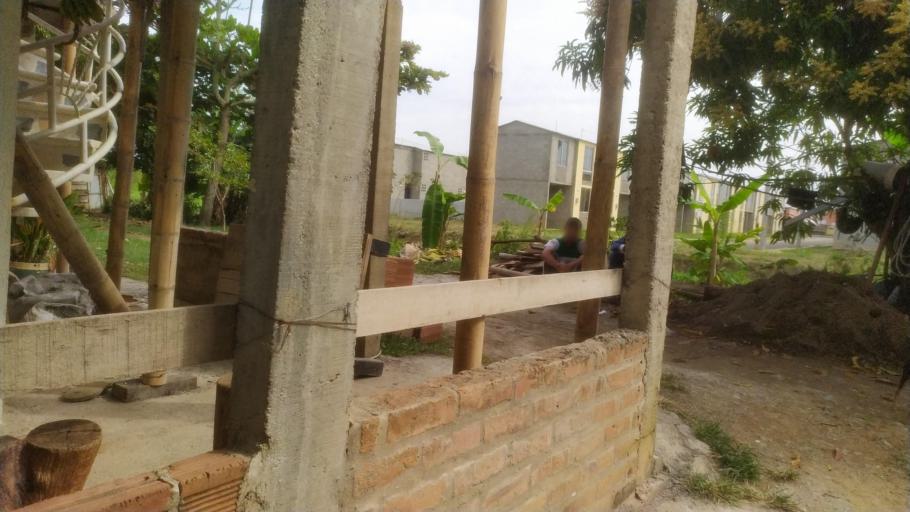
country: CO
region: Valle del Cauca
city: Jamundi
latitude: 3.2399
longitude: -76.5082
